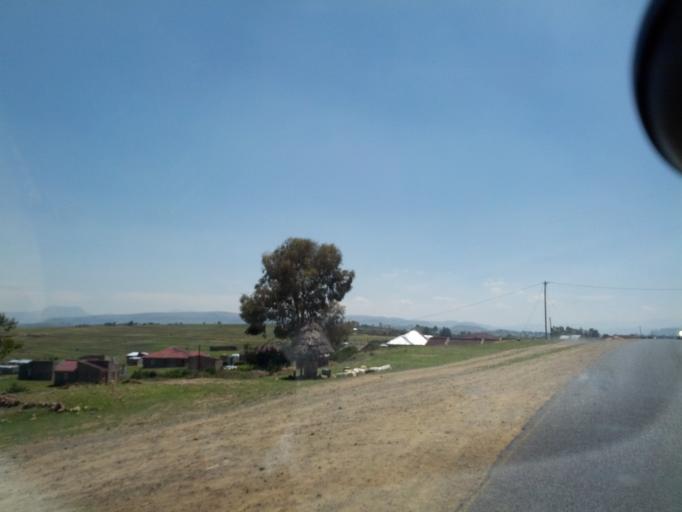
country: LS
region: Butha-Buthe
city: Butha-Buthe
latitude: -28.7824
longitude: 28.2240
